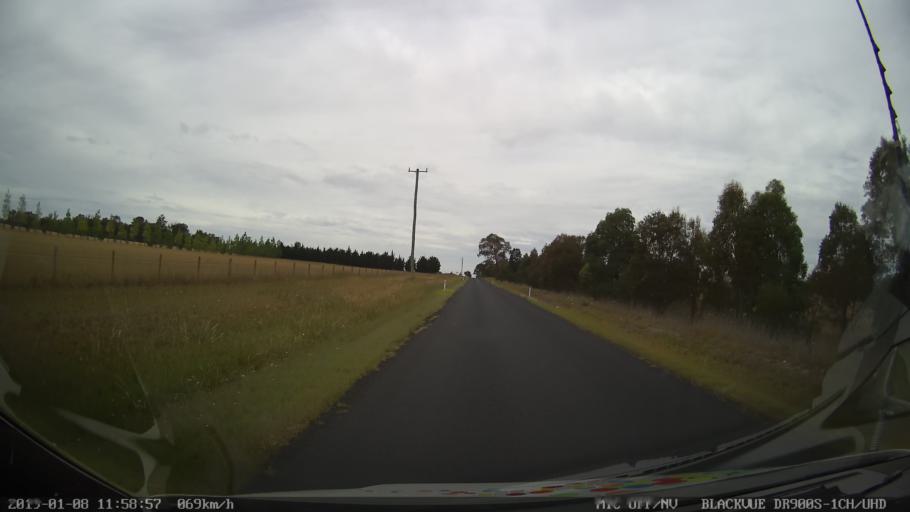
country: AU
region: New South Wales
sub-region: Armidale Dumaresq
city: Armidale
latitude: -30.4577
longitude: 151.5811
